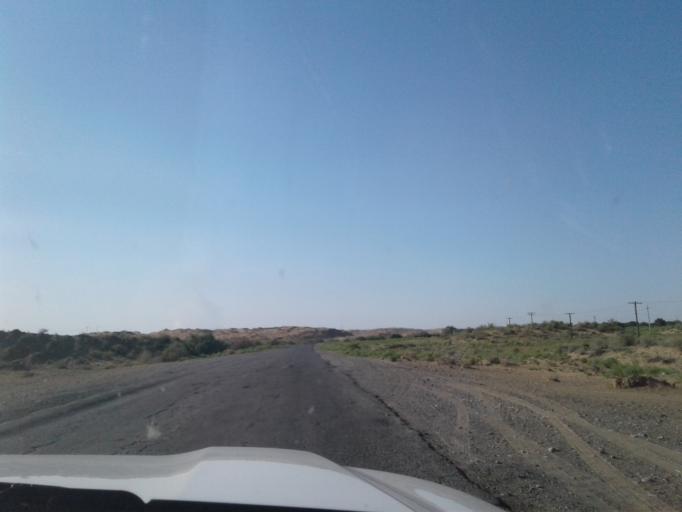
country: TM
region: Mary
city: Yoloeten
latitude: 36.9653
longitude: 62.4531
